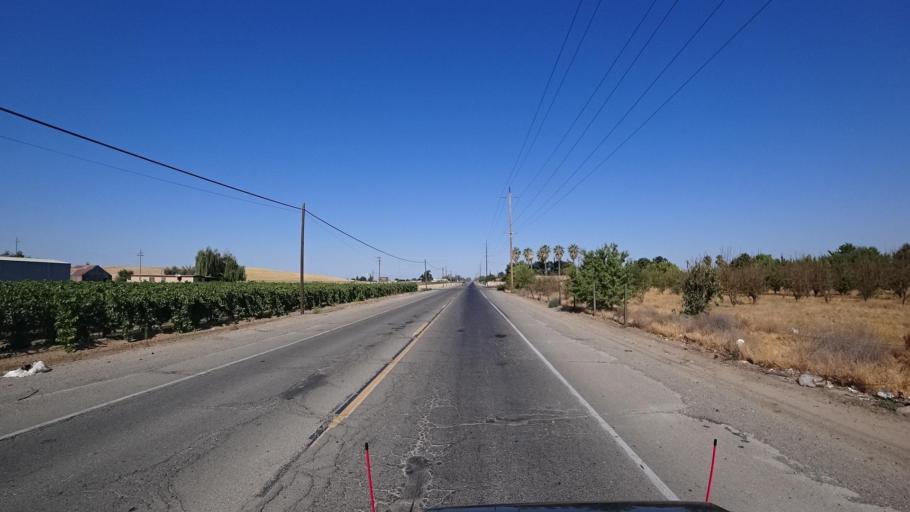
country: US
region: California
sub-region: Fresno County
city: West Park
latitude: 36.7068
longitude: -119.8256
